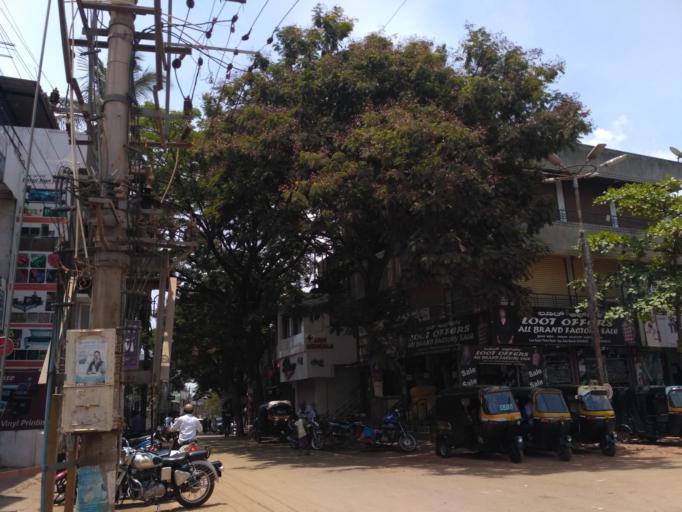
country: IN
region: Karnataka
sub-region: Dharwad
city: Hubli
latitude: 15.4562
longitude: 75.0114
